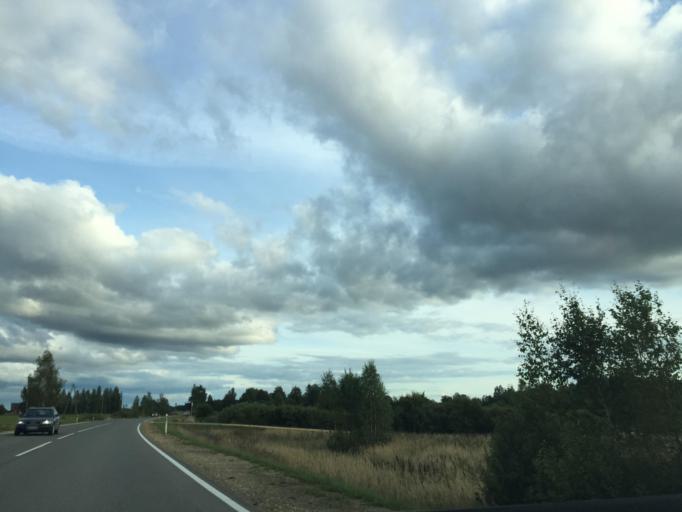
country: LV
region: Nereta
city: Nereta
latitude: 56.2379
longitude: 25.2687
